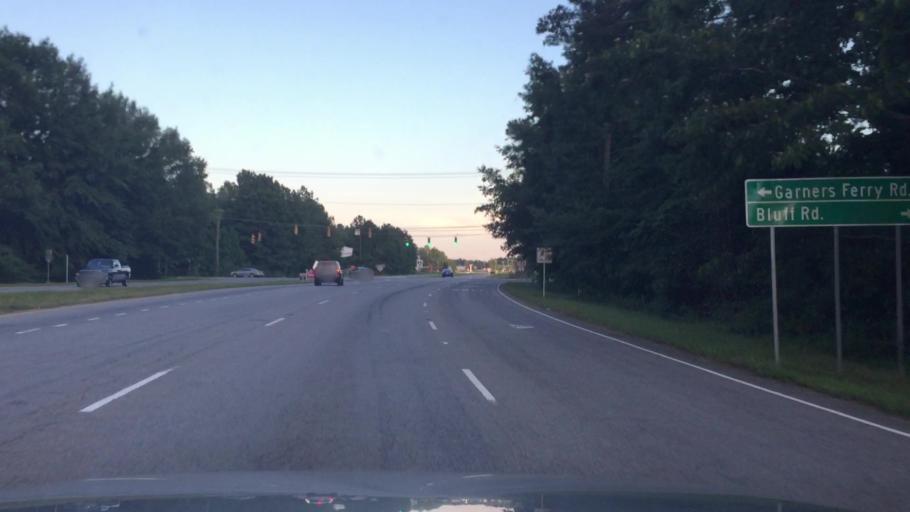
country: US
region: South Carolina
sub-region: Richland County
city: Forest Acres
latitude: 33.9489
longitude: -80.9662
